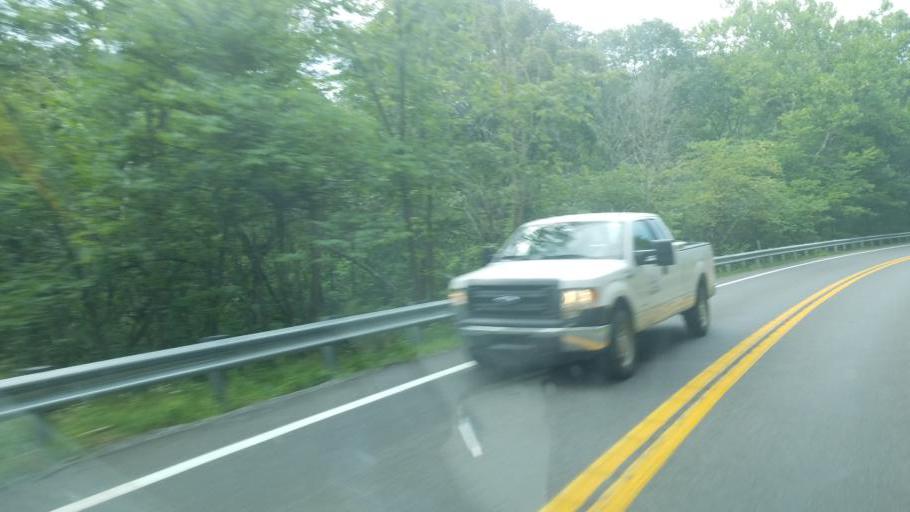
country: US
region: West Virginia
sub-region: Mineral County
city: Fort Ashby
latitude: 39.5409
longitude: -78.5012
